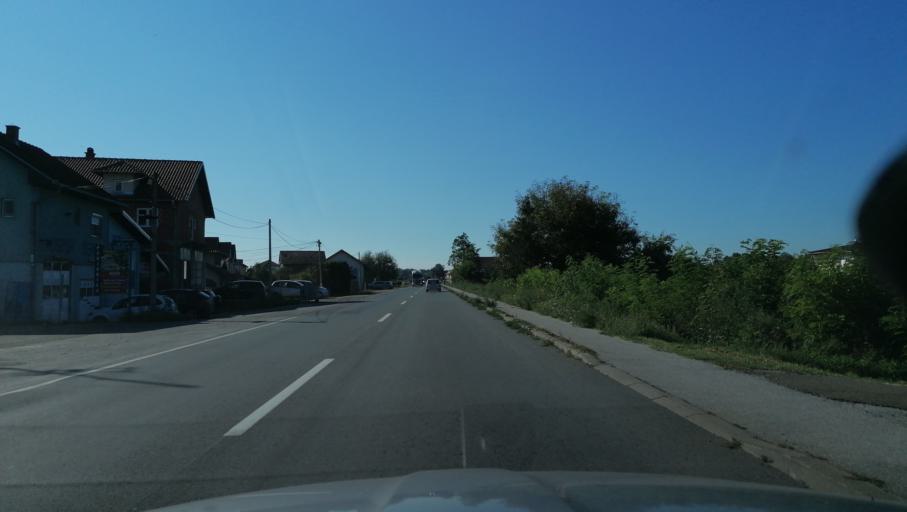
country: RS
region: Central Serbia
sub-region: Raski Okrug
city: Kraljevo
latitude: 43.7624
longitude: 20.6468
